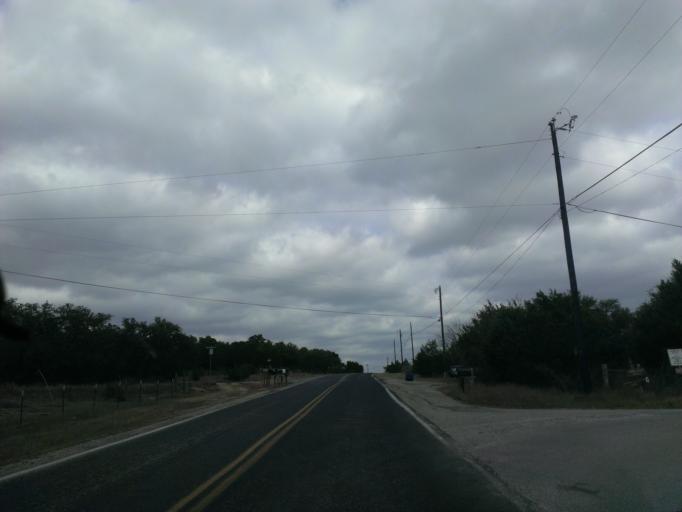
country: US
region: Texas
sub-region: Travis County
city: Briarcliff
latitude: 30.3778
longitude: -98.0940
